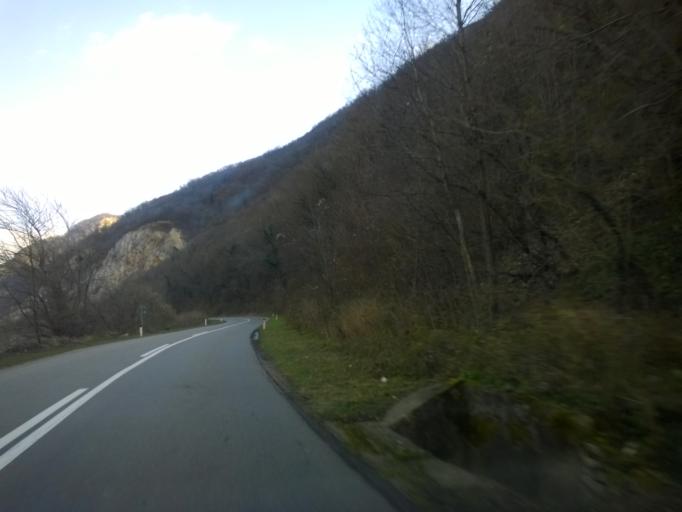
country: RO
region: Caras-Severin
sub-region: Comuna Pescari
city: Coronini
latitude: 44.6518
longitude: 21.7202
